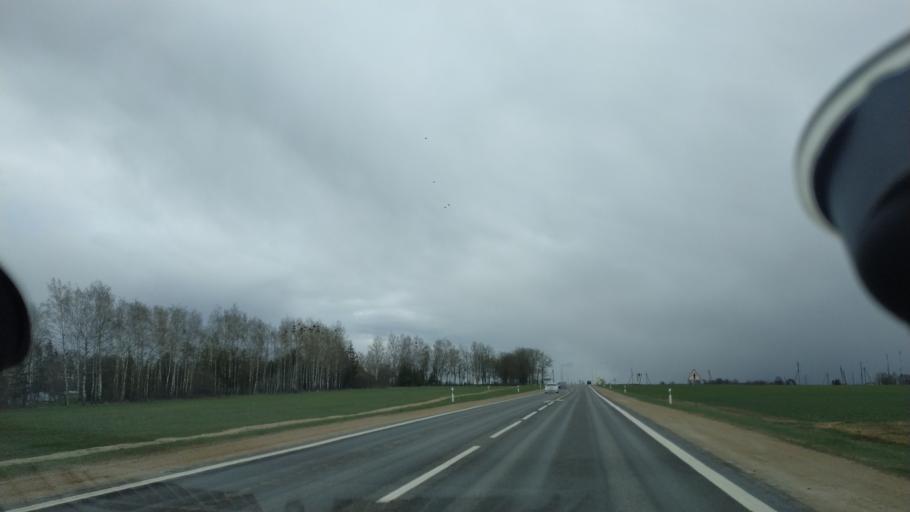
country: LT
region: Siauliu apskritis
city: Pakruojis
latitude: 55.7992
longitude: 24.0116
